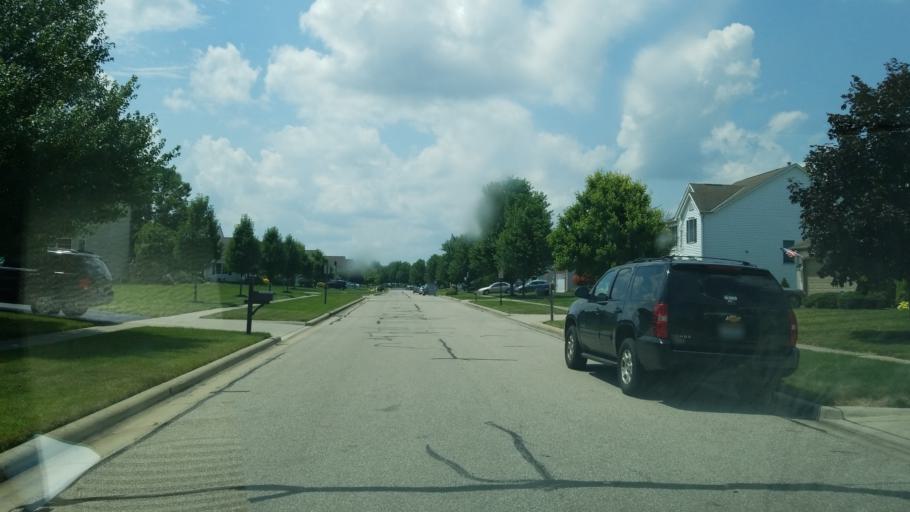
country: US
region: Ohio
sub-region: Delaware County
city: Lewis Center
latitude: 40.2199
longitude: -82.9953
